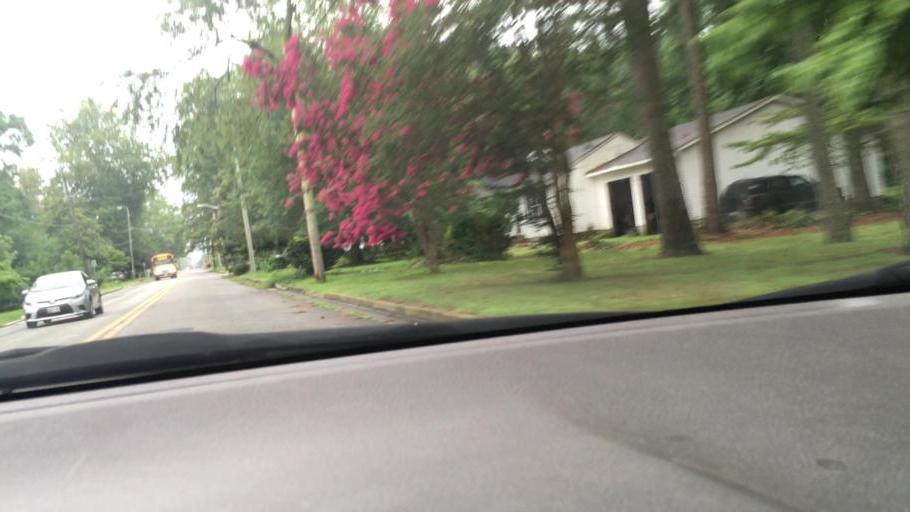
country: US
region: Maryland
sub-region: Wicomico County
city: Fruitland
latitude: 38.3310
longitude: -75.6258
